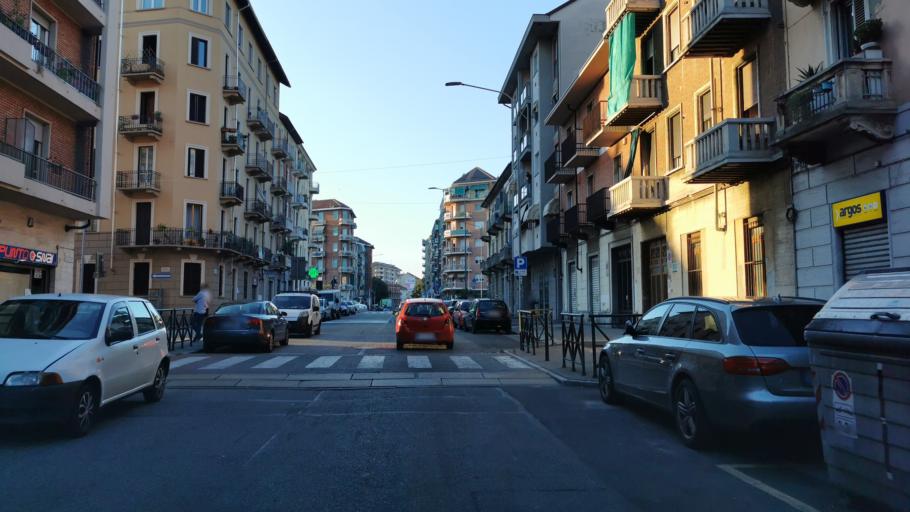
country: IT
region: Piedmont
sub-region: Provincia di Torino
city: Turin
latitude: 45.0977
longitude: 7.6940
